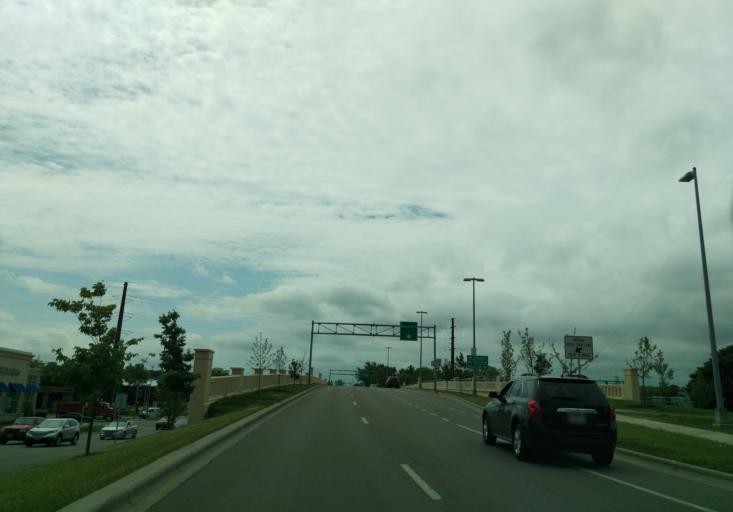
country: US
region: Wisconsin
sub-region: Dane County
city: Middleton
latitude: 43.0614
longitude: -89.5275
